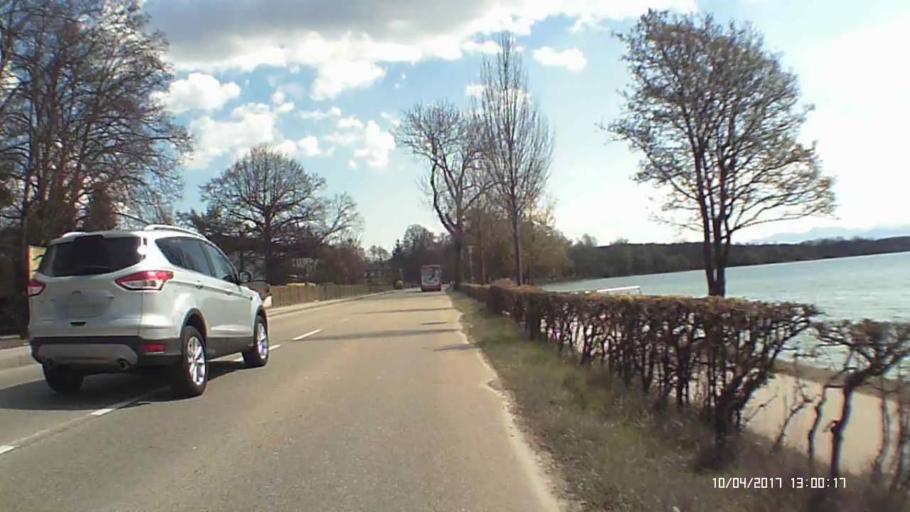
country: DE
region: Bavaria
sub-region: Upper Bavaria
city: Seeon-Seebruck
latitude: 47.9332
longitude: 12.4833
